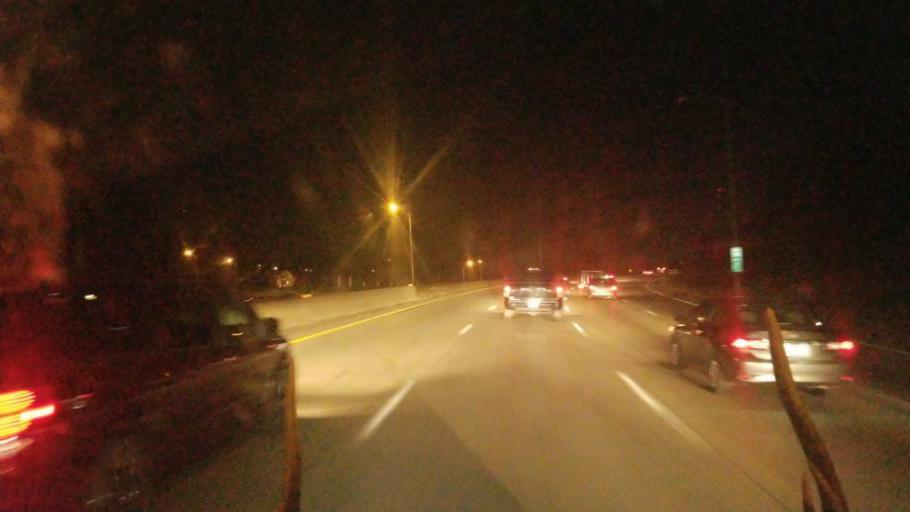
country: US
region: Missouri
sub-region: Jackson County
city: Kansas City
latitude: 39.0969
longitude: -94.5478
